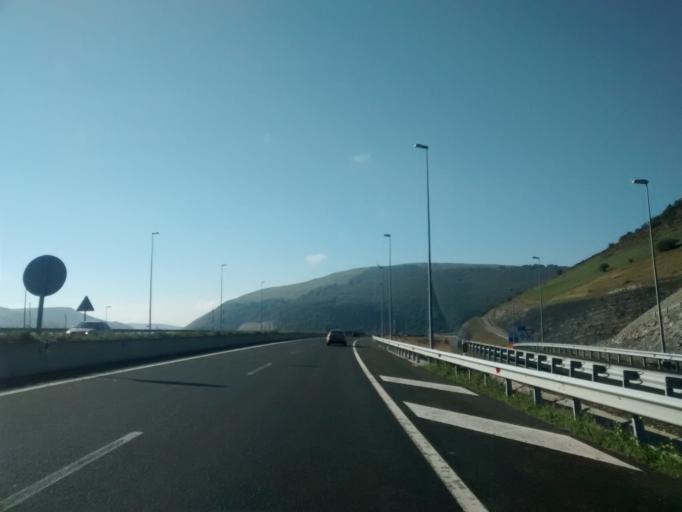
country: ES
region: Cantabria
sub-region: Provincia de Cantabria
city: Santiurde de Reinosa
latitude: 43.0704
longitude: -4.0863
